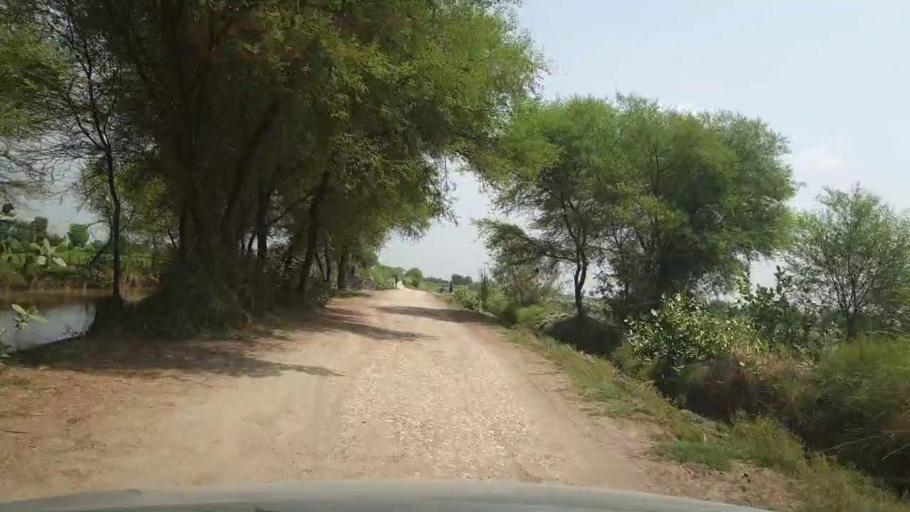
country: PK
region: Sindh
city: Garhi Yasin
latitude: 27.9380
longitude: 68.3686
